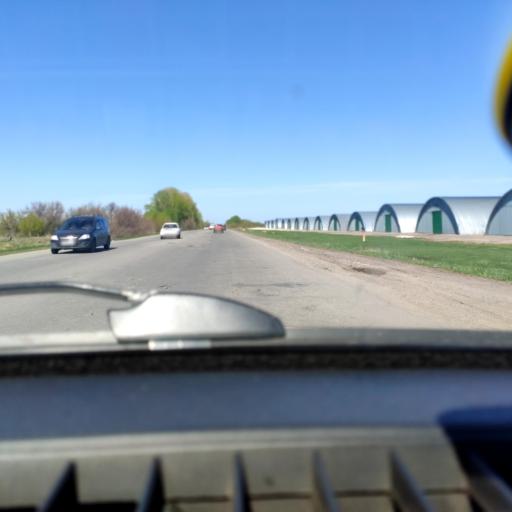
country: RU
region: Samara
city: Tol'yatti
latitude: 53.6860
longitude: 49.4172
